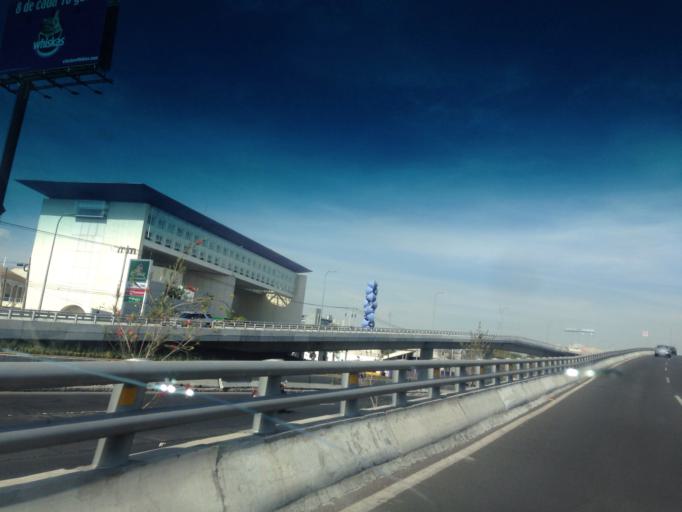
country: MX
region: Mexico City
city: Tlalpan
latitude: 19.2862
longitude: -99.1481
